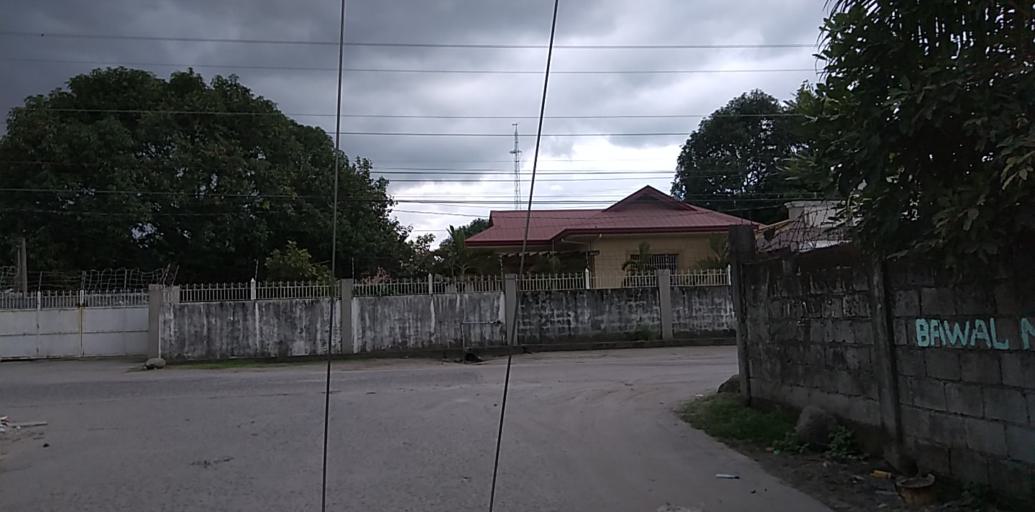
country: PH
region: Central Luzon
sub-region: Province of Pampanga
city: Pio
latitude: 15.0478
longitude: 120.5311
